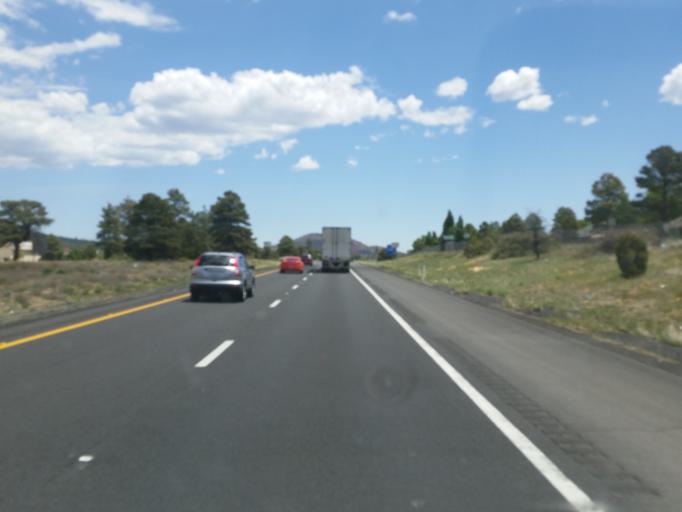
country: US
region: Arizona
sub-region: Coconino County
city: Flagstaff
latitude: 35.2069
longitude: -111.6011
